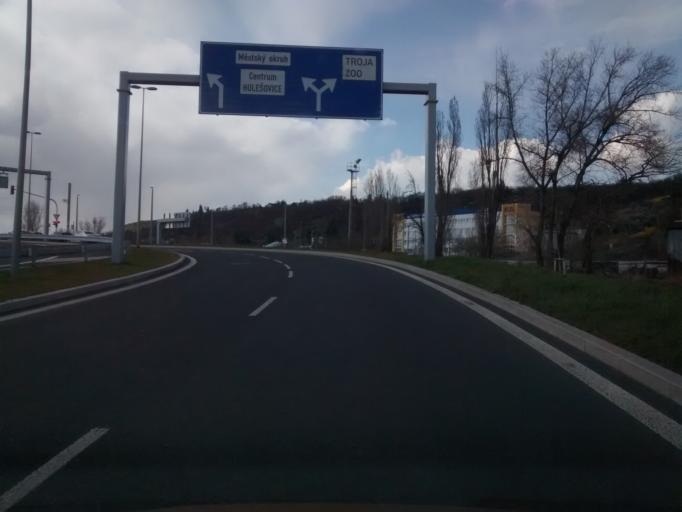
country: CZ
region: Praha
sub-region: Praha 8
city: Karlin
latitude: 50.1146
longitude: 14.4365
